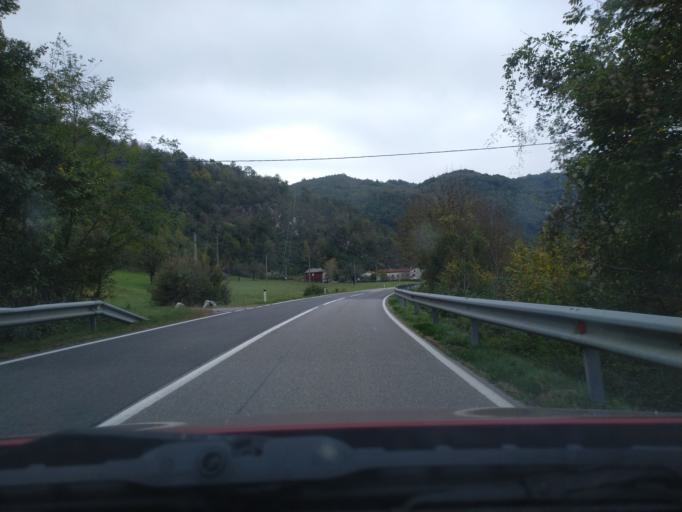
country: SI
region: Kanal
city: Deskle
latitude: 46.0339
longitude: 13.5988
